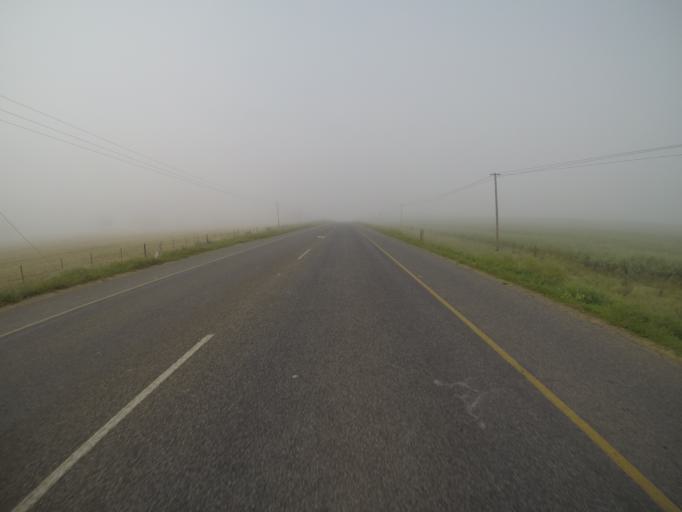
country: ZA
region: Western Cape
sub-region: City of Cape Town
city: Kraaifontein
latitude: -33.6778
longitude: 18.7063
